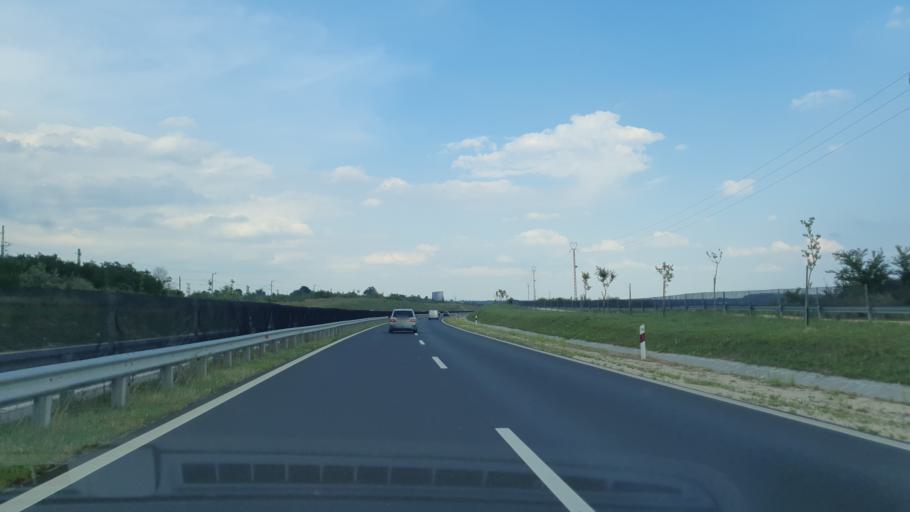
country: HU
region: Veszprem
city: Varpalota
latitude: 47.1956
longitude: 18.1591
